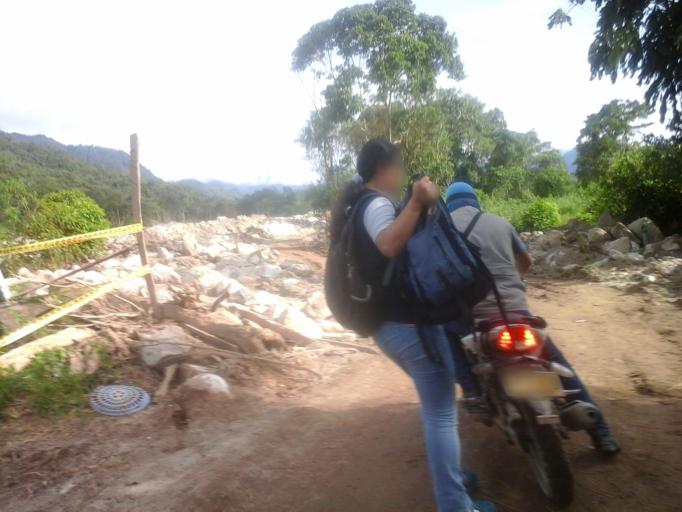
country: CO
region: Putumayo
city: Mocoa
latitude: 1.1682
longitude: -76.6608
